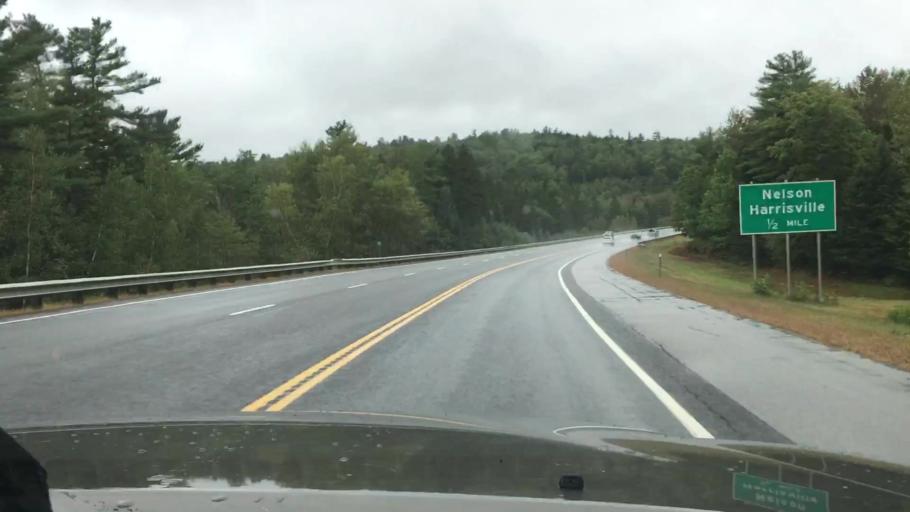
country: US
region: New Hampshire
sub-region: Cheshire County
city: Harrisville
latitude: 43.0046
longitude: -72.1536
